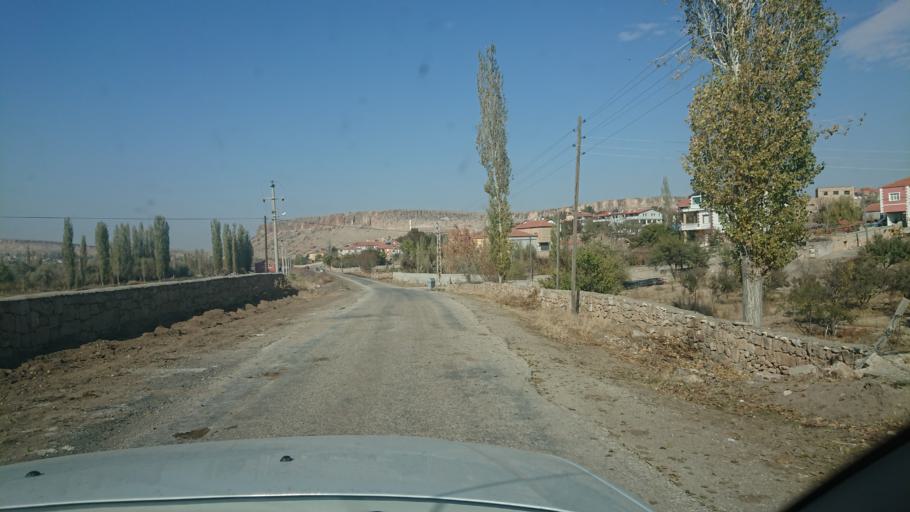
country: TR
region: Aksaray
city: Gulagac
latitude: 38.3515
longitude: 34.2343
